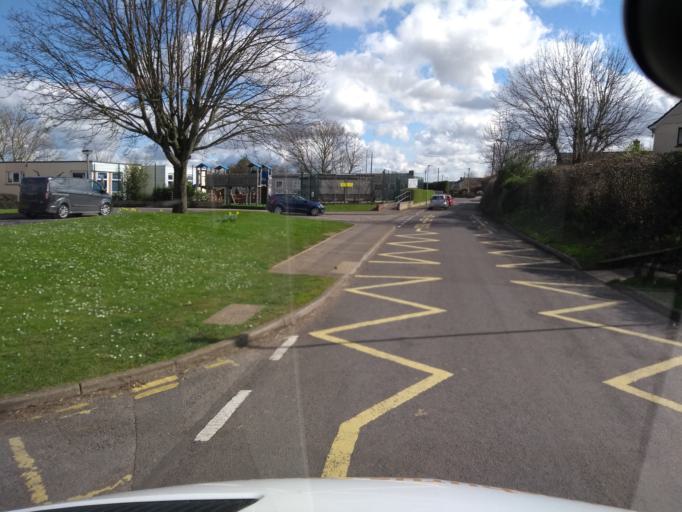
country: GB
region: England
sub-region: Somerset
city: Creech Saint Michael
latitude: 51.0279
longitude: -3.0430
